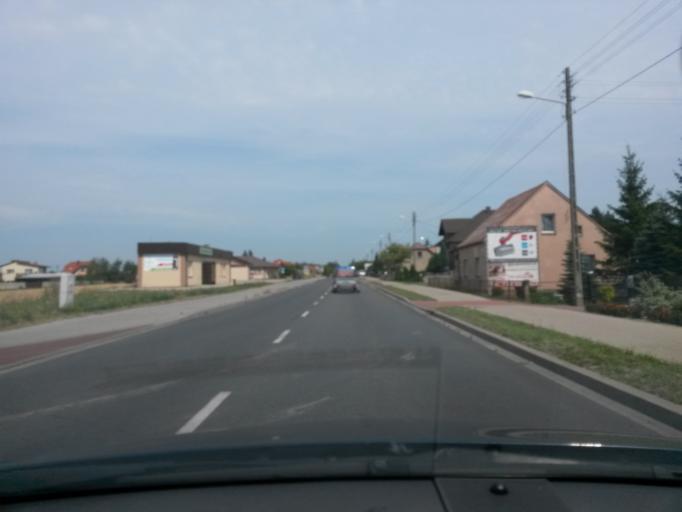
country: PL
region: Greater Poland Voivodeship
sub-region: Powiat gostynski
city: Krobia
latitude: 51.7659
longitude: 16.9717
